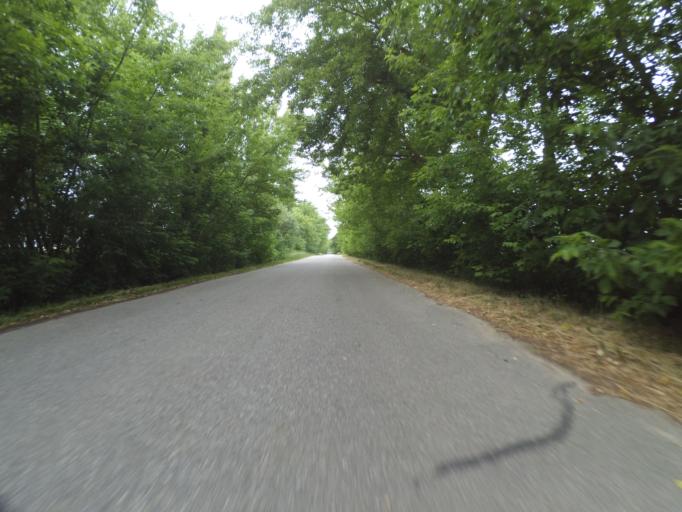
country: DE
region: Mecklenburg-Vorpommern
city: Lubz
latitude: 53.5166
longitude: 12.0309
